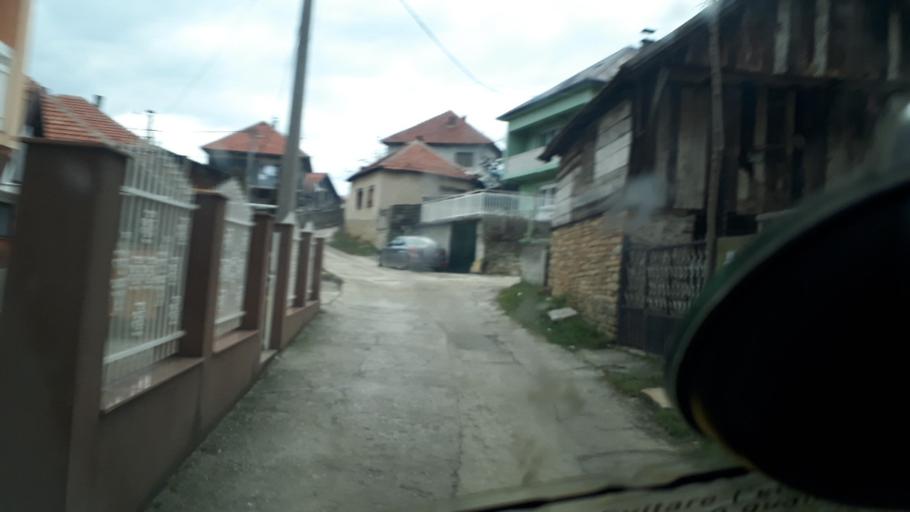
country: BA
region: Federation of Bosnia and Herzegovina
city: Zenica
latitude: 44.1506
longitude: 17.9716
